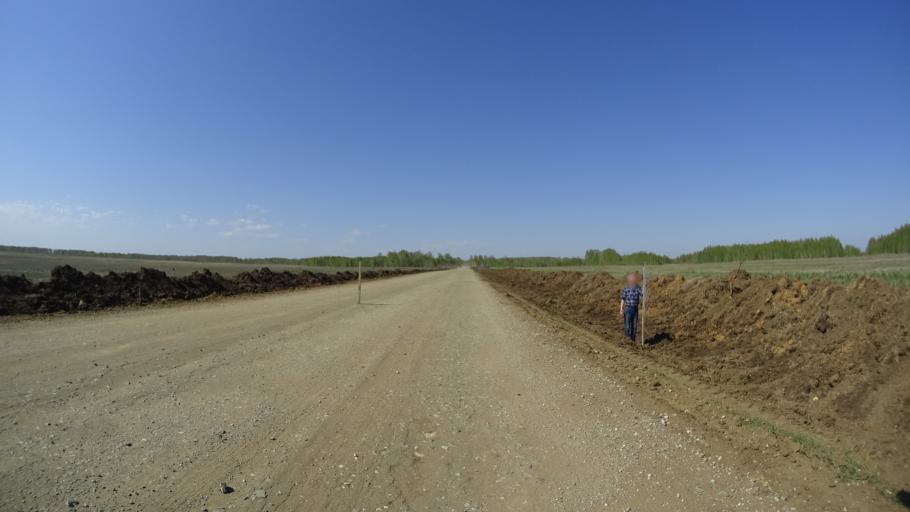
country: RU
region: Chelyabinsk
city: Troitsk
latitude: 54.1807
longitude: 61.4768
